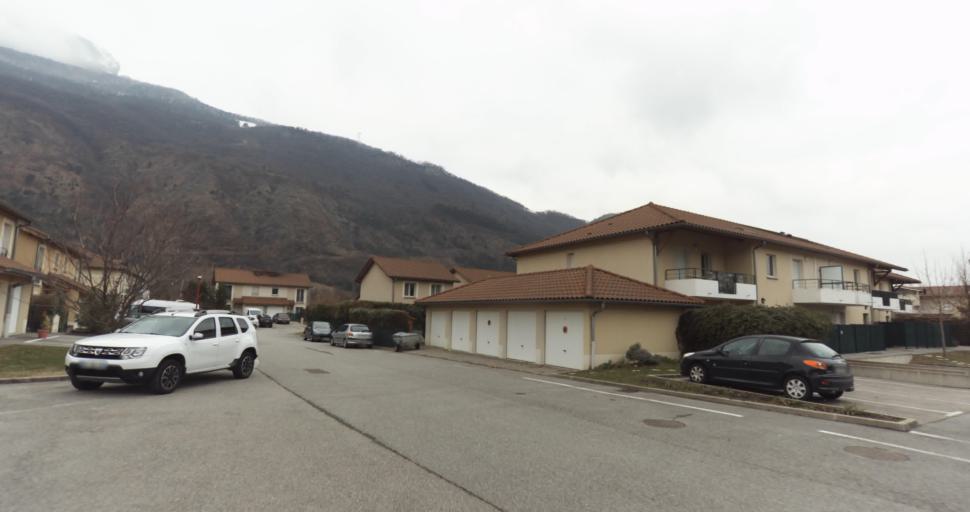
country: FR
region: Rhone-Alpes
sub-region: Departement de l'Isere
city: Vif
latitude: 45.0496
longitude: 5.6668
